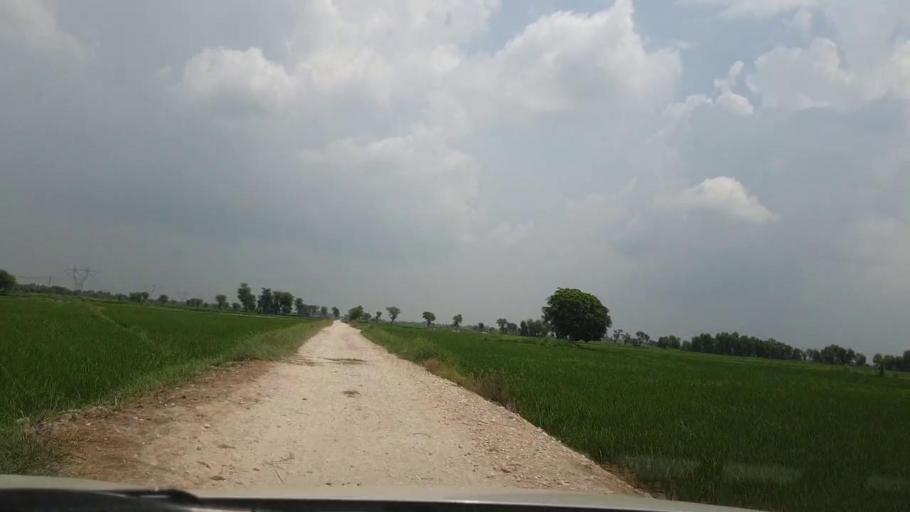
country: PK
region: Sindh
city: Goth Garelo
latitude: 27.4131
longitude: 68.0711
